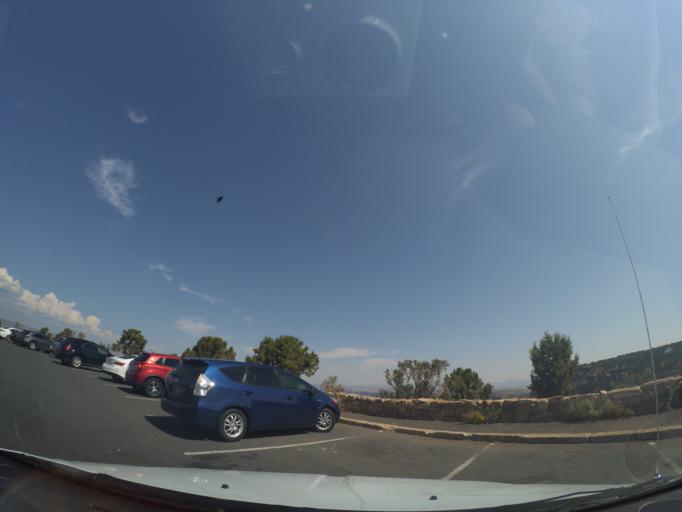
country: US
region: Arizona
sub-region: Coconino County
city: Grand Canyon
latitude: 36.0381
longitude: -111.8371
